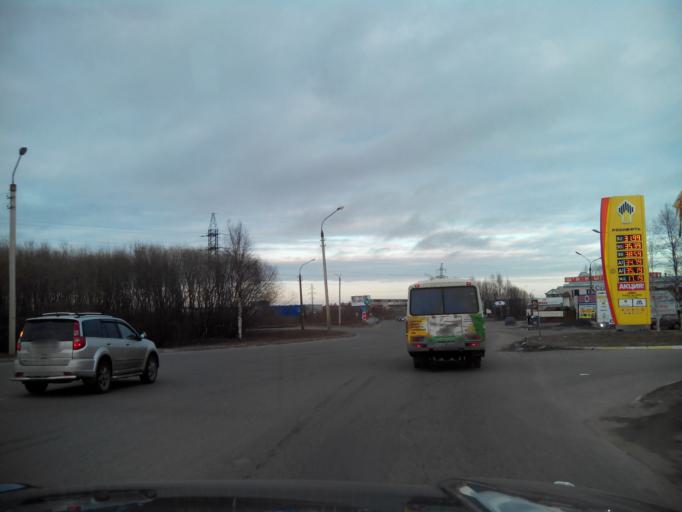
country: RU
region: Arkhangelskaya
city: Arkhangel'sk
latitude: 64.5662
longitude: 40.5669
